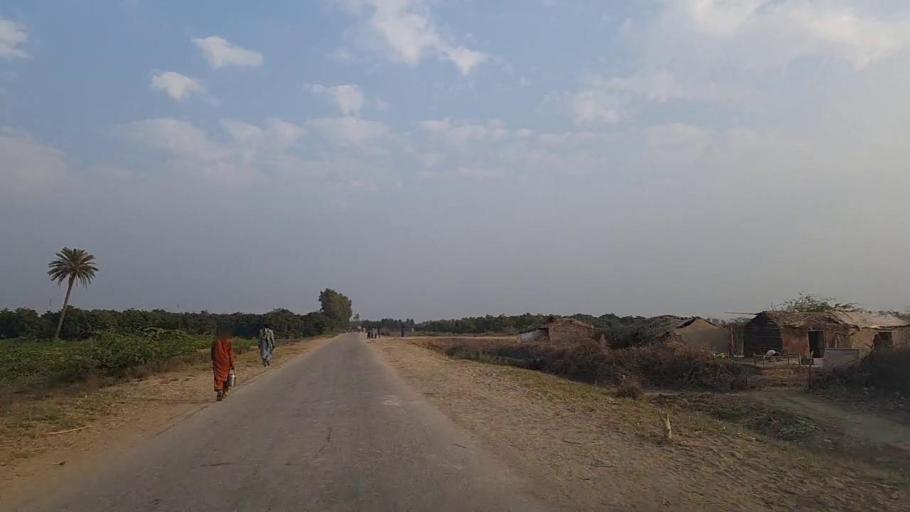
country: PK
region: Sindh
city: Samaro
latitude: 25.2895
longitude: 69.2353
